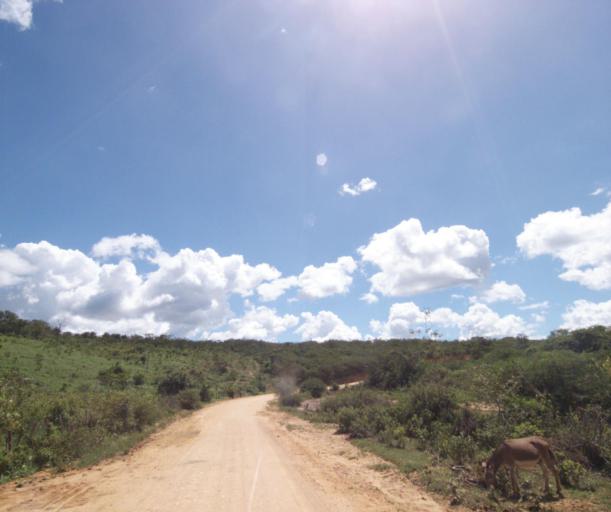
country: BR
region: Bahia
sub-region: Pocoes
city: Pocoes
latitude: -14.2992
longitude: -40.6411
